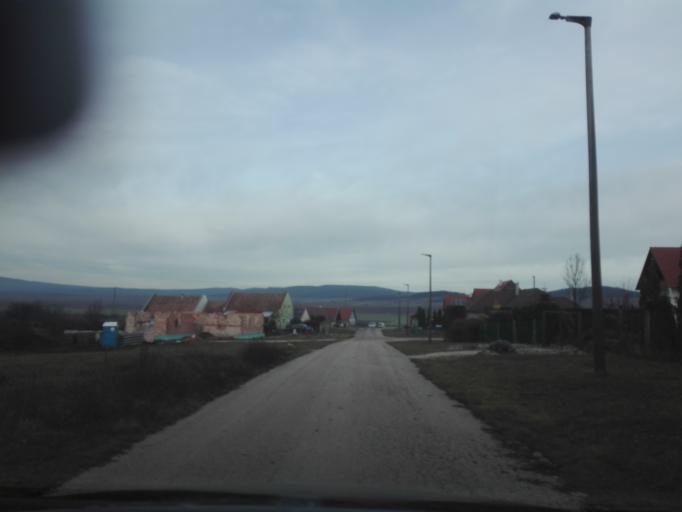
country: HU
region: Veszprem
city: Balatonfured
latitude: 47.0093
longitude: 17.7805
